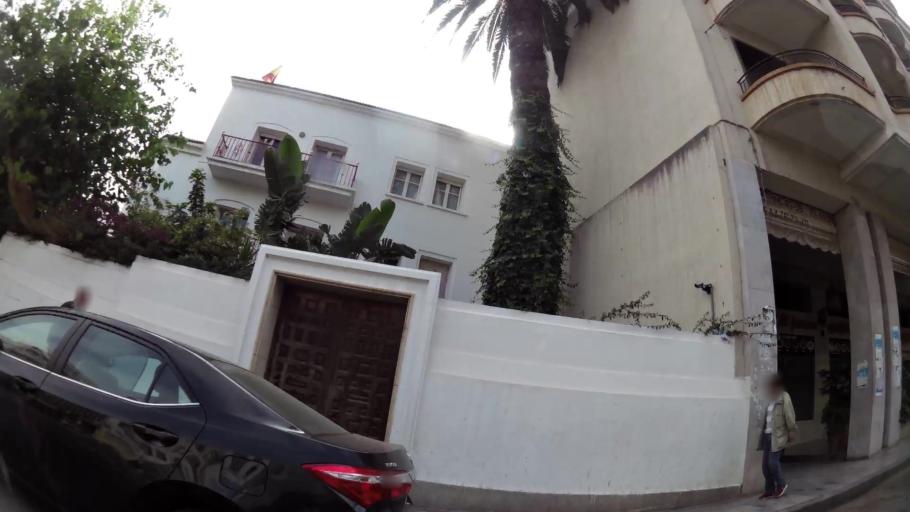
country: MA
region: Rabat-Sale-Zemmour-Zaer
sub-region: Rabat
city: Rabat
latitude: 34.0183
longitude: -6.8342
